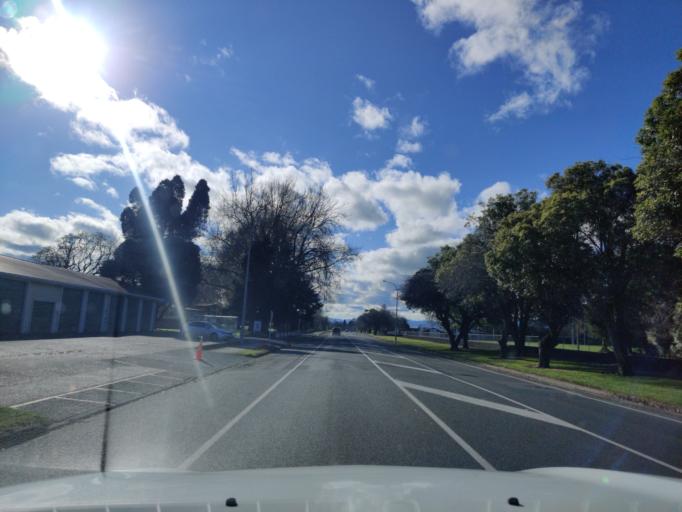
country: NZ
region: Waikato
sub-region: Matamata-Piako District
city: Matamata
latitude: -37.8178
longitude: 175.7711
